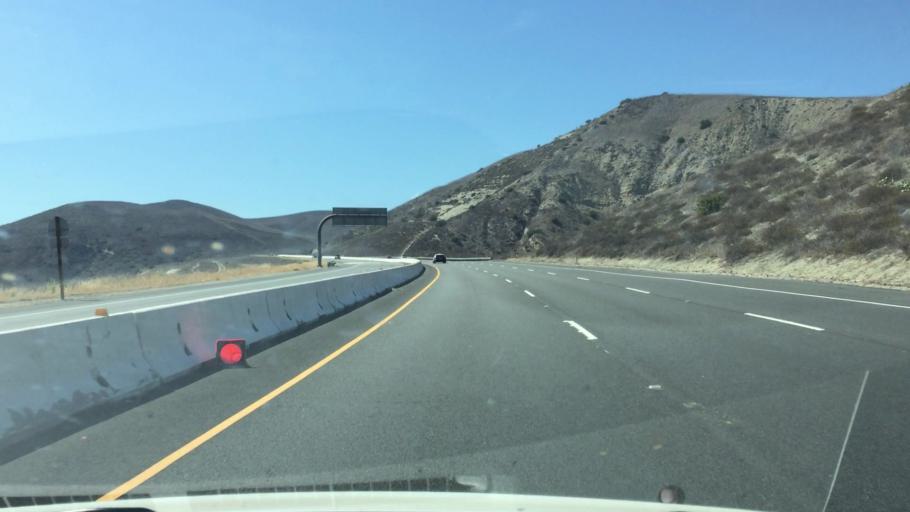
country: US
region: California
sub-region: Orange County
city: North Tustin
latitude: 33.7464
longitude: -117.7214
